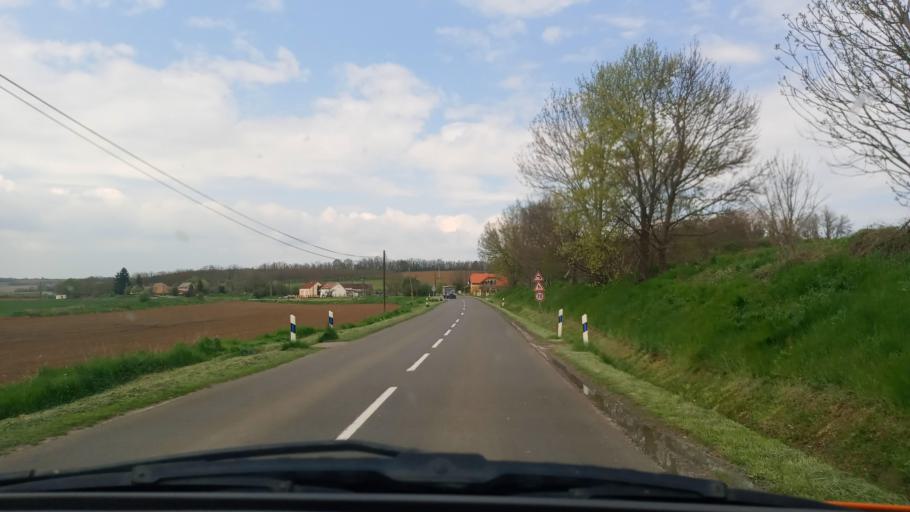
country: HU
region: Baranya
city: Sasd
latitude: 46.2625
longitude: 18.0901
